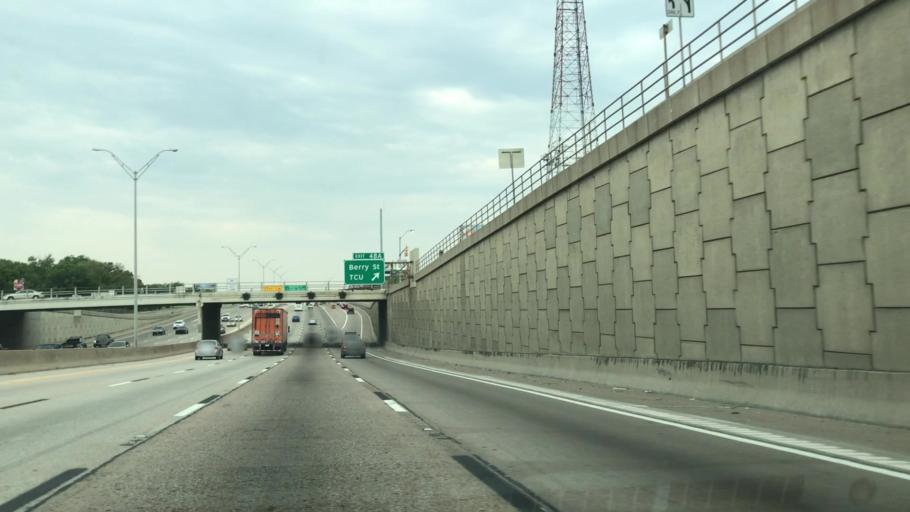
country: US
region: Texas
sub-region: Tarrant County
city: Fort Worth
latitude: 32.7143
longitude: -97.3207
